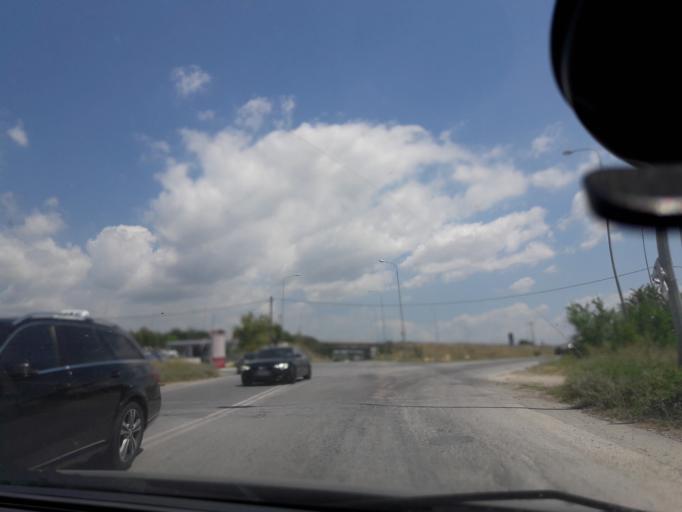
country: GR
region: Central Macedonia
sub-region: Nomos Chalkidikis
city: Nea Kallikrateia
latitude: 40.3178
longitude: 23.0866
